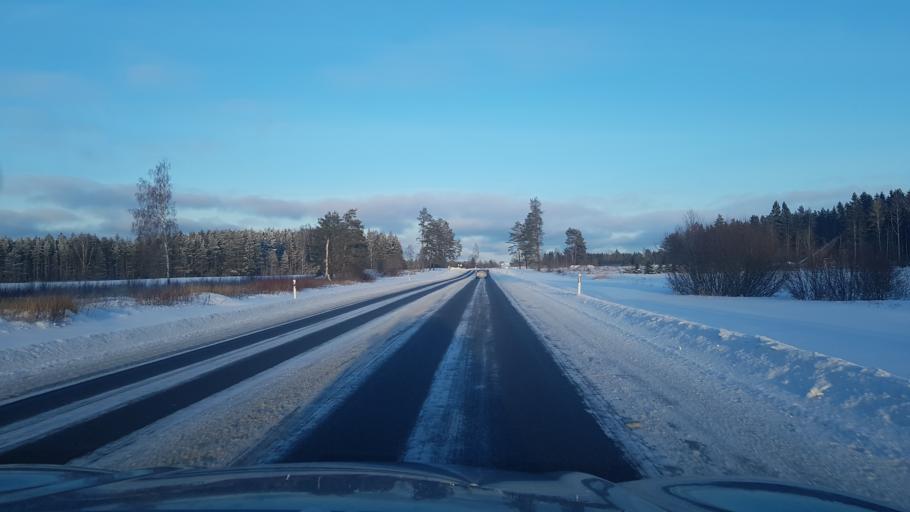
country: EE
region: Ida-Virumaa
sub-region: Toila vald
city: Voka
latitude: 59.3865
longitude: 27.5728
